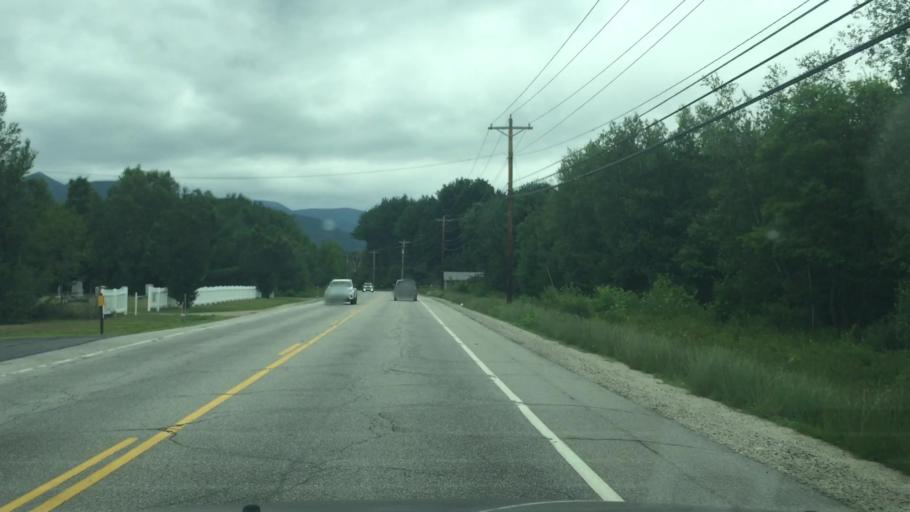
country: US
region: New Hampshire
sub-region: Carroll County
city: North Conway
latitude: 44.0806
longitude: -71.2532
